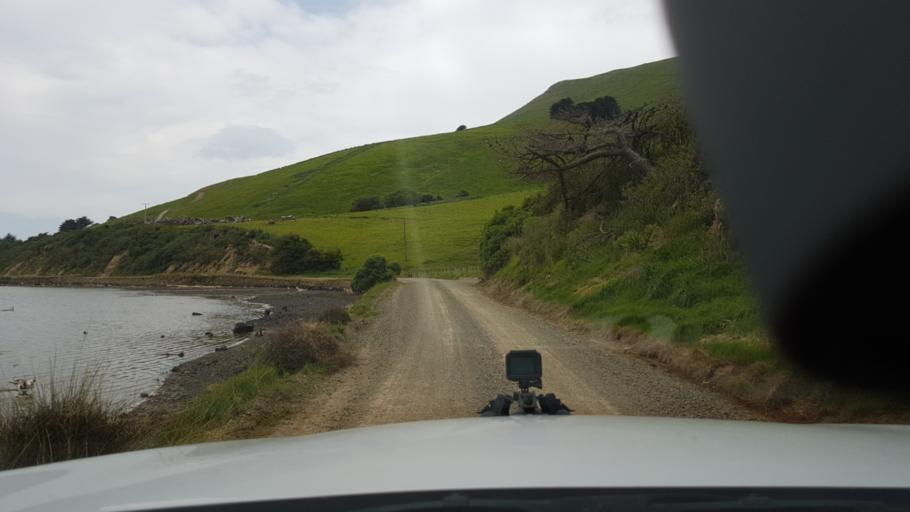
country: NZ
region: Otago
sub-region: Dunedin City
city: Portobello
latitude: -45.8547
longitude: 170.6935
